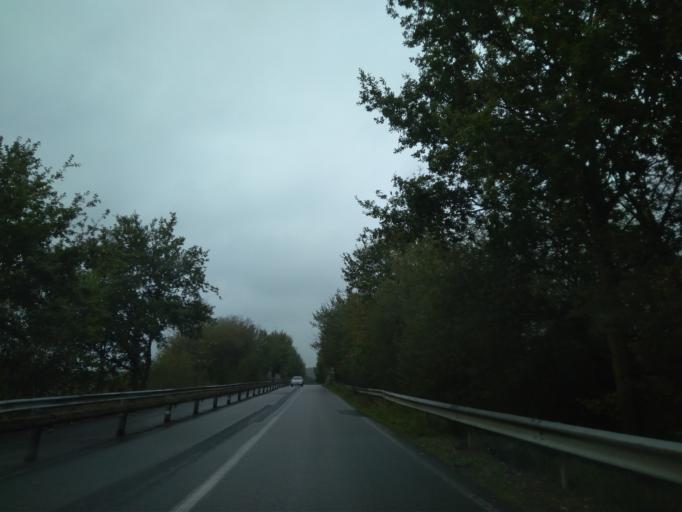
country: FR
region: Brittany
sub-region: Departement d'Ille-et-Vilaine
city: Saint-Gregoire
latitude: 48.1465
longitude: -1.6688
